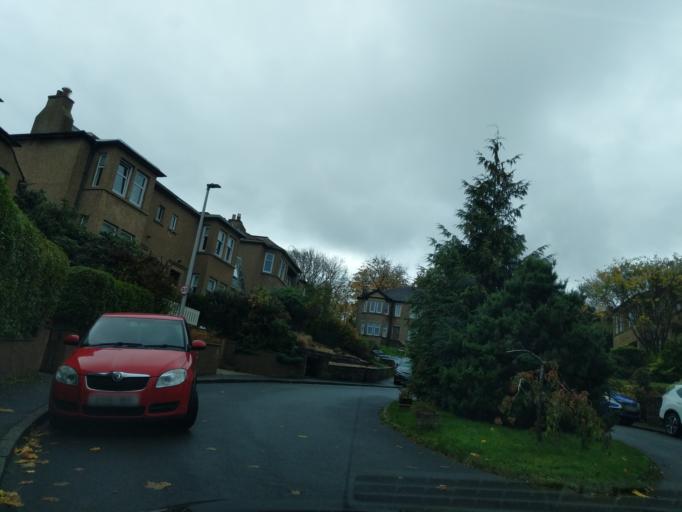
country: GB
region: Scotland
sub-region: Edinburgh
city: Colinton
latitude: 55.9114
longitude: -3.2627
